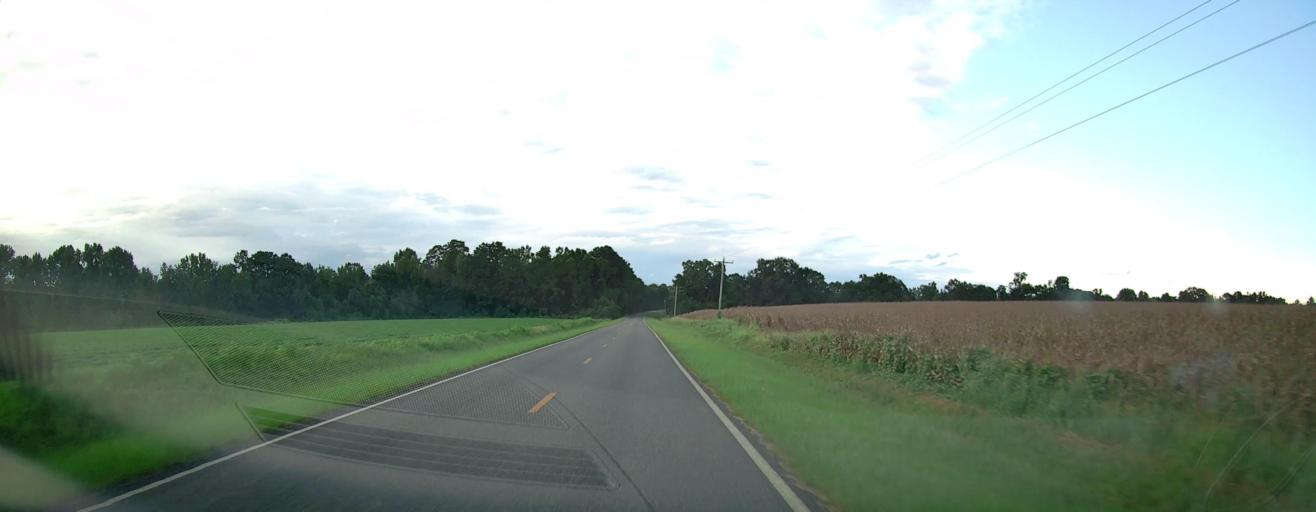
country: US
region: Georgia
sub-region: Pulaski County
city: Hawkinsville
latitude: 32.3074
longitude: -83.5529
